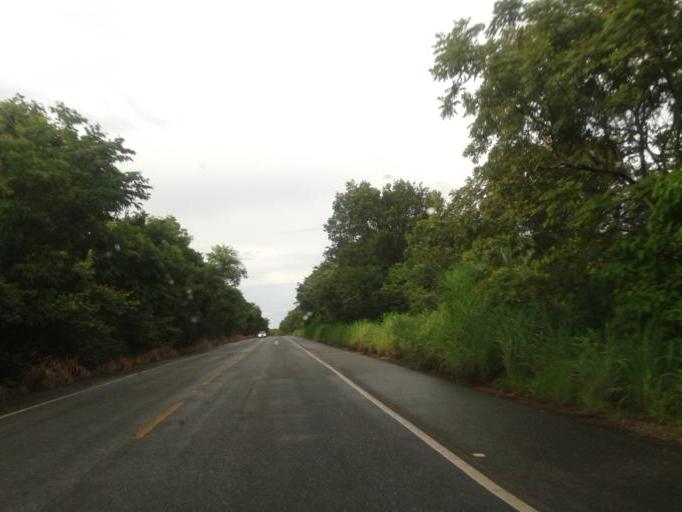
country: BR
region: Goias
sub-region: Mozarlandia
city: Mozarlandia
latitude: -14.8677
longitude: -50.5496
